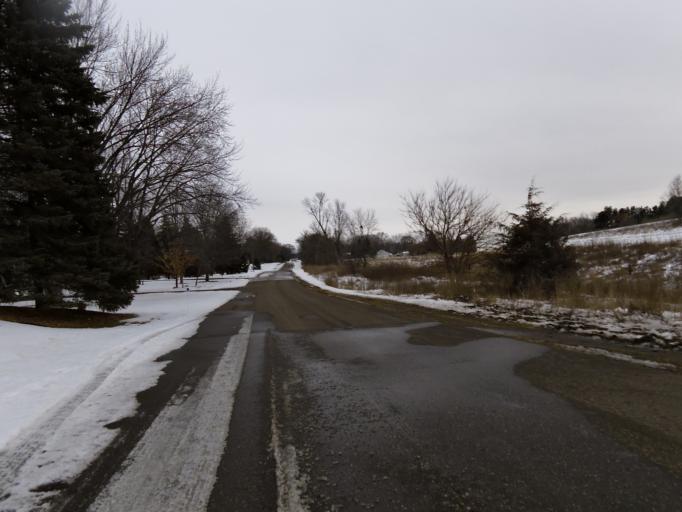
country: US
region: Minnesota
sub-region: Washington County
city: Lakeland
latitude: 44.9589
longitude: -92.7706
